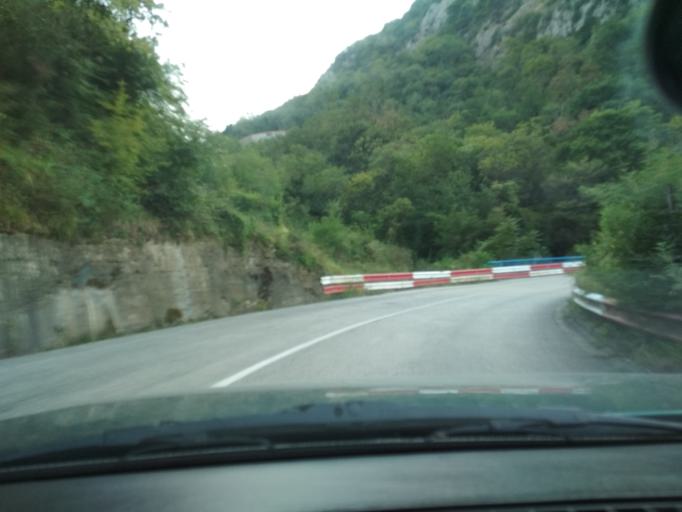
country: ME
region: Kotor
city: Kotor
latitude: 42.4083
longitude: 18.7665
